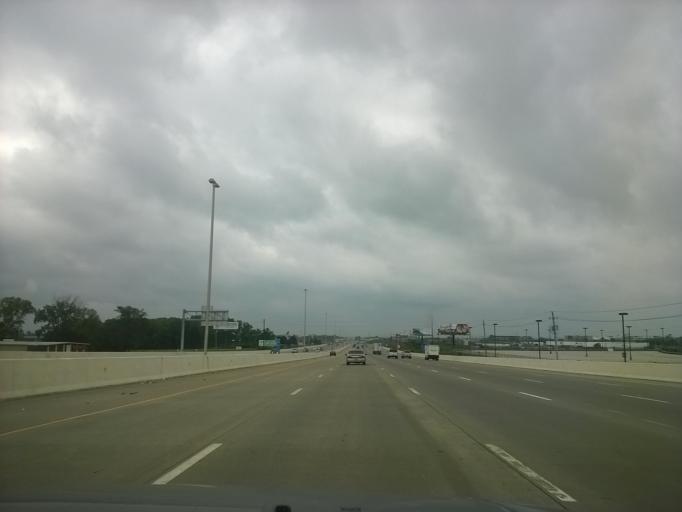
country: US
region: Indiana
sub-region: Marion County
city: Speedway
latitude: 39.7423
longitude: -86.2647
